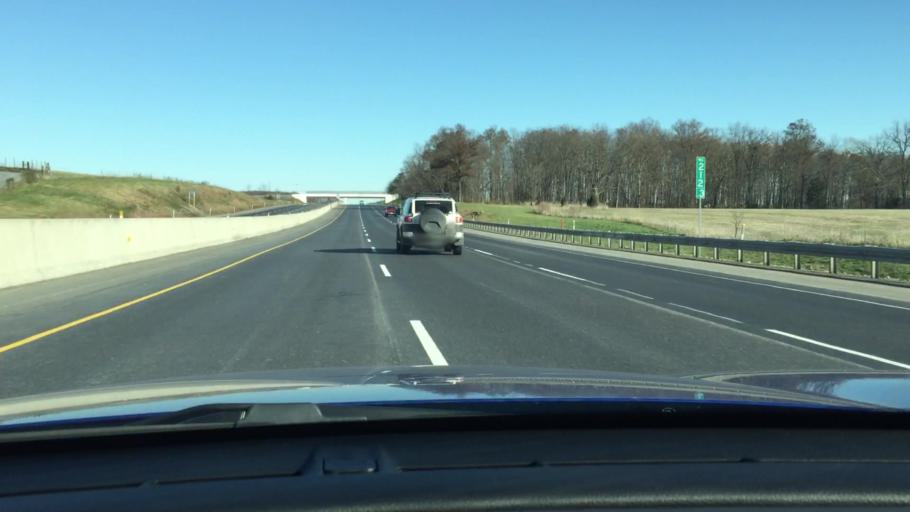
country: US
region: Pennsylvania
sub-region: Cumberland County
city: Newville
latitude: 40.1958
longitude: -77.4154
